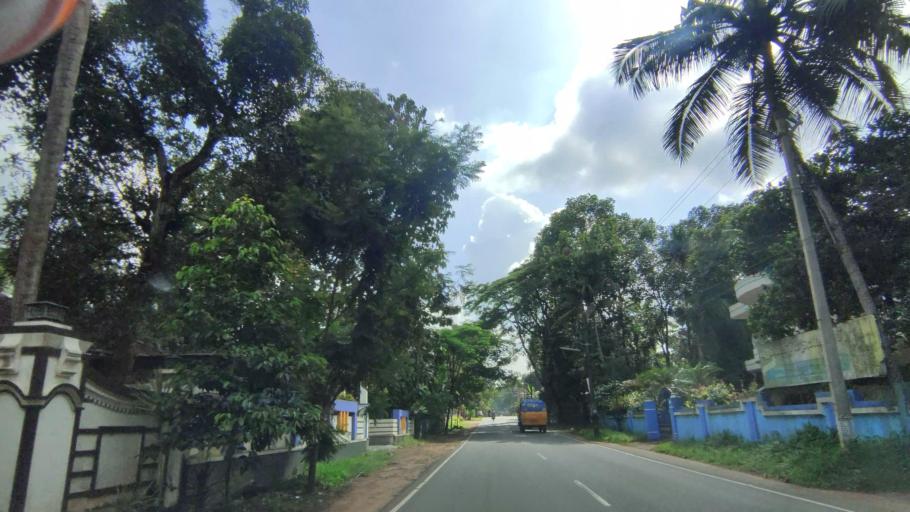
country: IN
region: Kerala
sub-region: Kottayam
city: Kottayam
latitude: 9.6750
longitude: 76.5361
